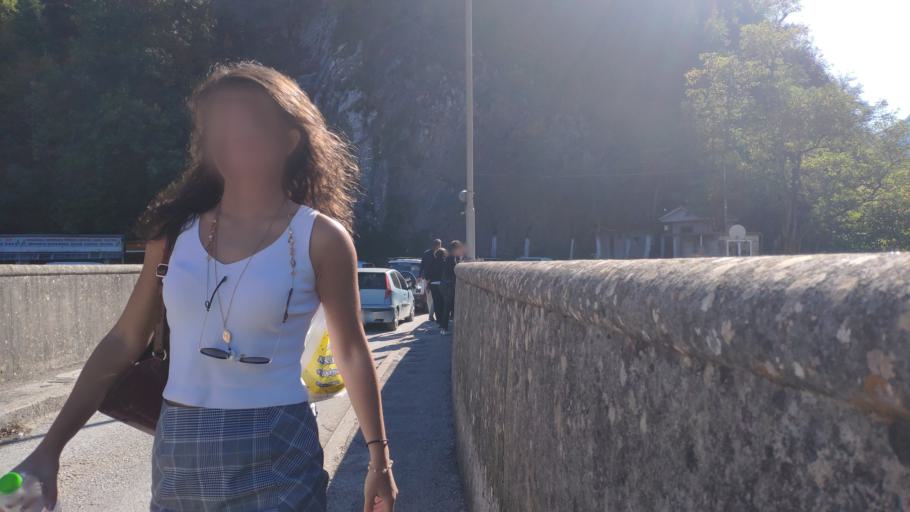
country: GR
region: Thessaly
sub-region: Nomos Kardhitsas
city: Neochori
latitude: 39.2355
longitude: 21.7465
